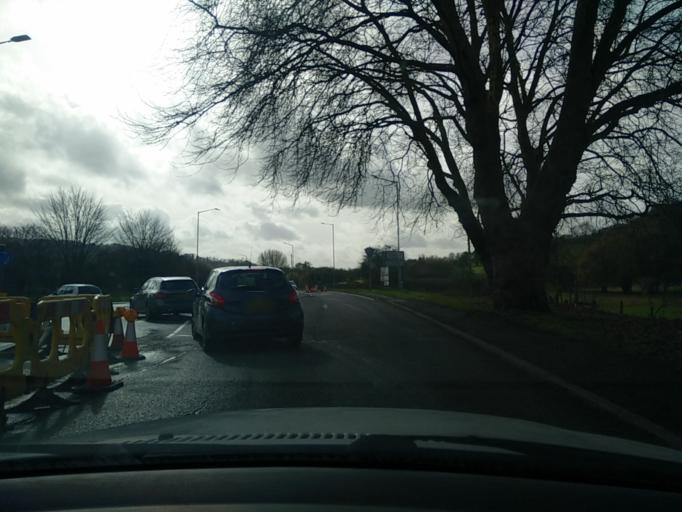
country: GB
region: England
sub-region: Buckinghamshire
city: High Wycombe
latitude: 51.6597
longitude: -0.7515
